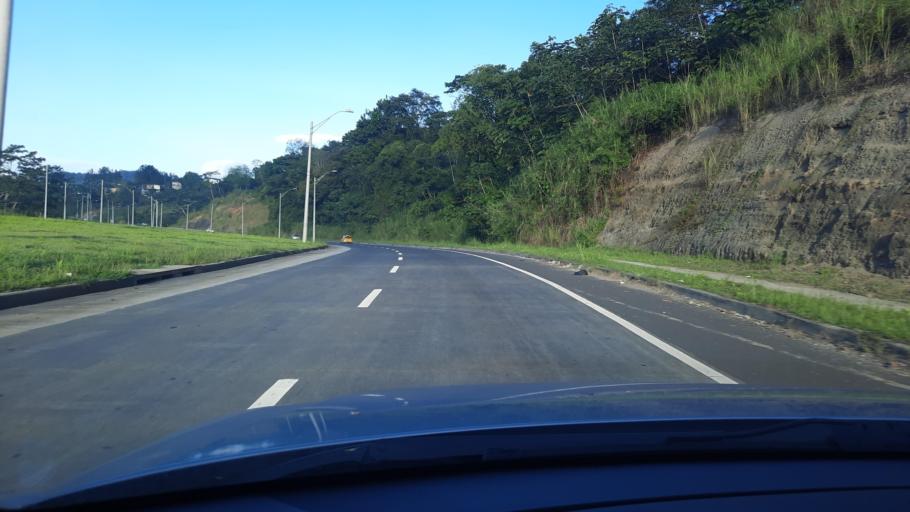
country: PA
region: Panama
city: Las Cumbres
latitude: 9.1042
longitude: -79.5263
